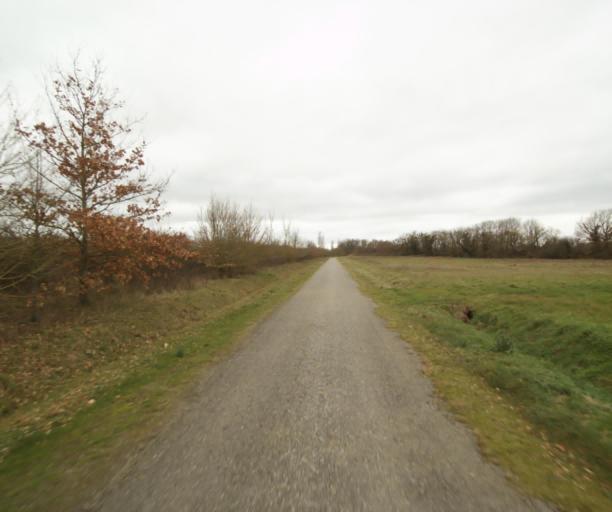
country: FR
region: Midi-Pyrenees
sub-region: Departement de l'Ariege
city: Saverdun
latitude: 43.1848
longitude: 1.6257
